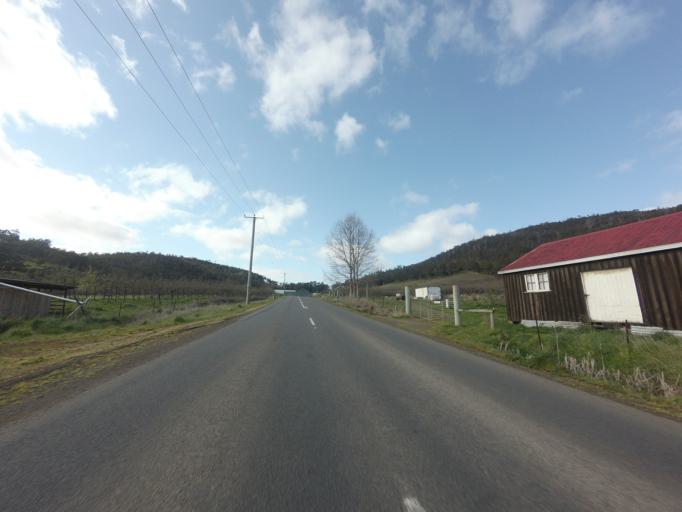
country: AU
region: Tasmania
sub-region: Huon Valley
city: Geeveston
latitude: -43.1712
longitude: 146.9432
